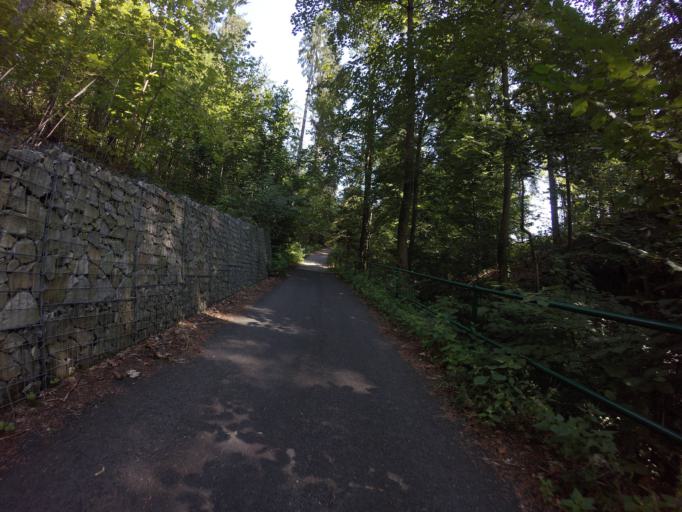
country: CZ
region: Jihocesky
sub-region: Okres Cesky Krumlov
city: Cesky Krumlov
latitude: 48.8604
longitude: 14.3765
